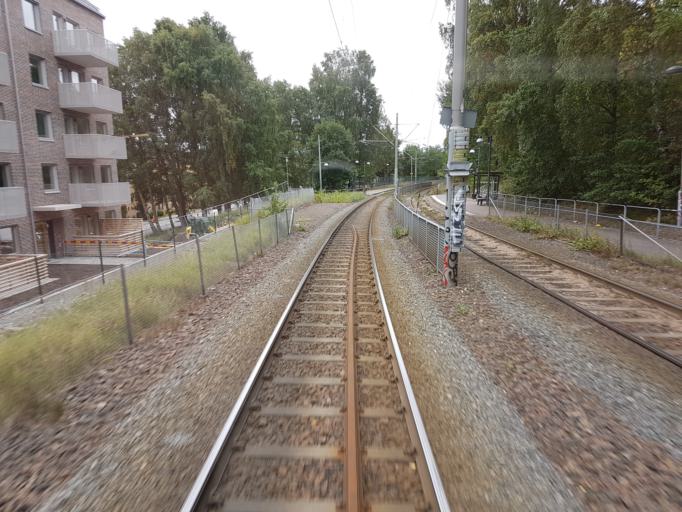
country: SE
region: Vaestra Goetaland
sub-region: Goteborg
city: Majorna
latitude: 57.6630
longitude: 11.9252
